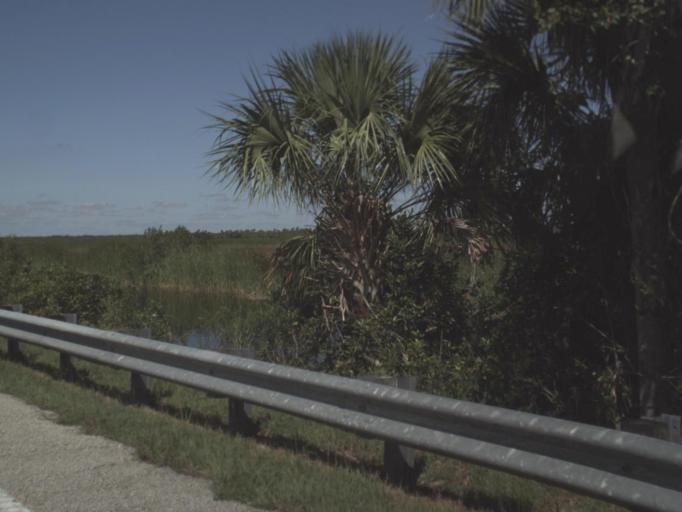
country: US
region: Florida
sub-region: Collier County
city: Marco
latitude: 25.9197
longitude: -81.4008
